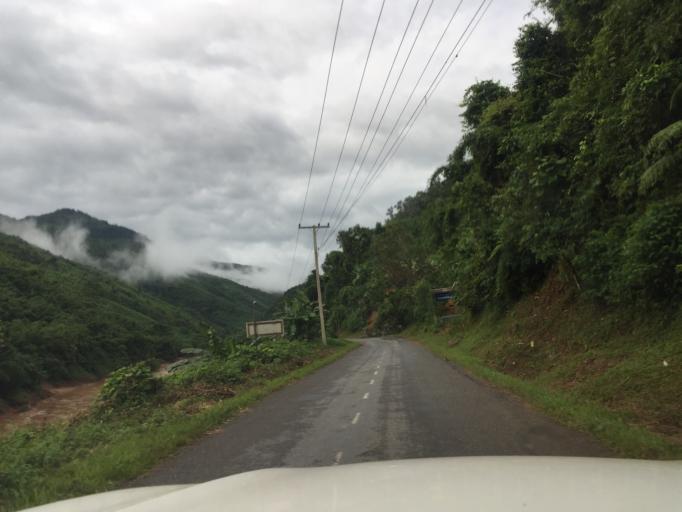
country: LA
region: Oudomxai
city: Muang La
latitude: 21.0511
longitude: 102.2412
